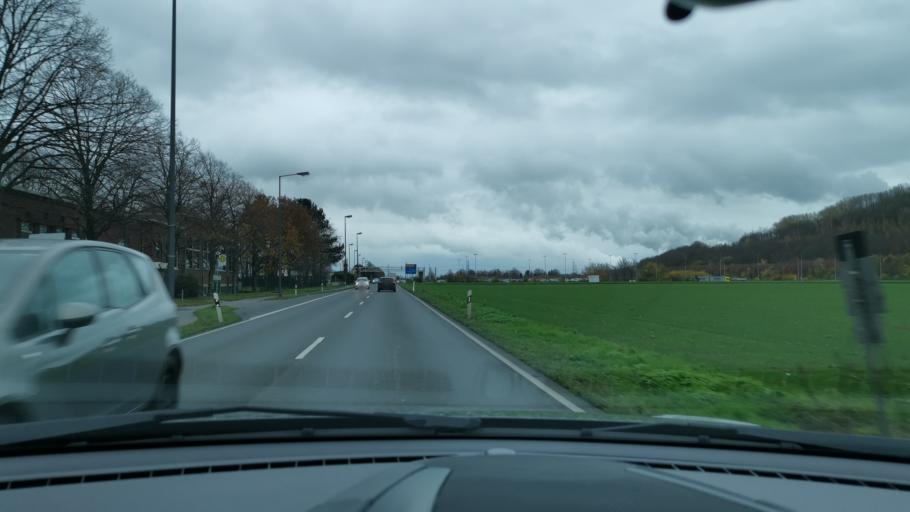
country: DE
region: North Rhine-Westphalia
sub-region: Regierungsbezirk Dusseldorf
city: Grevenbroich
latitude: 51.0779
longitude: 6.6176
